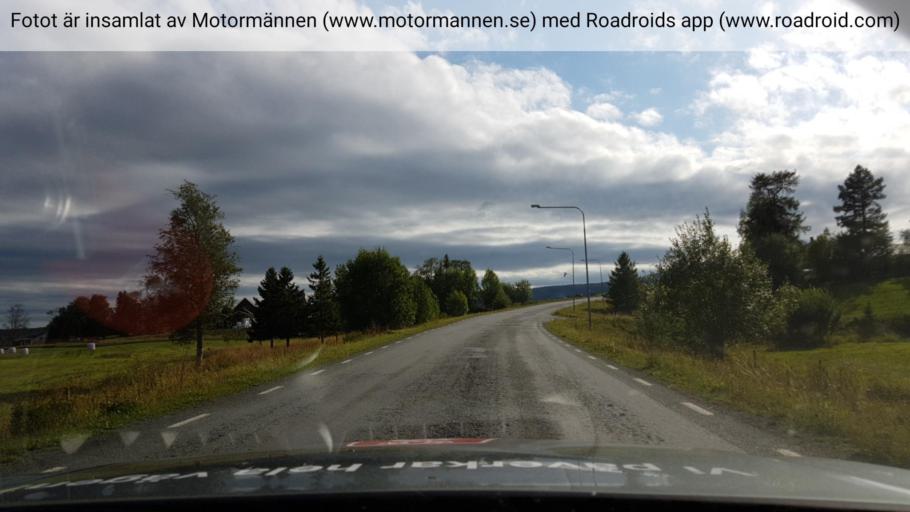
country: SE
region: Jaemtland
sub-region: Krokoms Kommun
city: Valla
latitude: 63.4547
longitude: 14.0609
